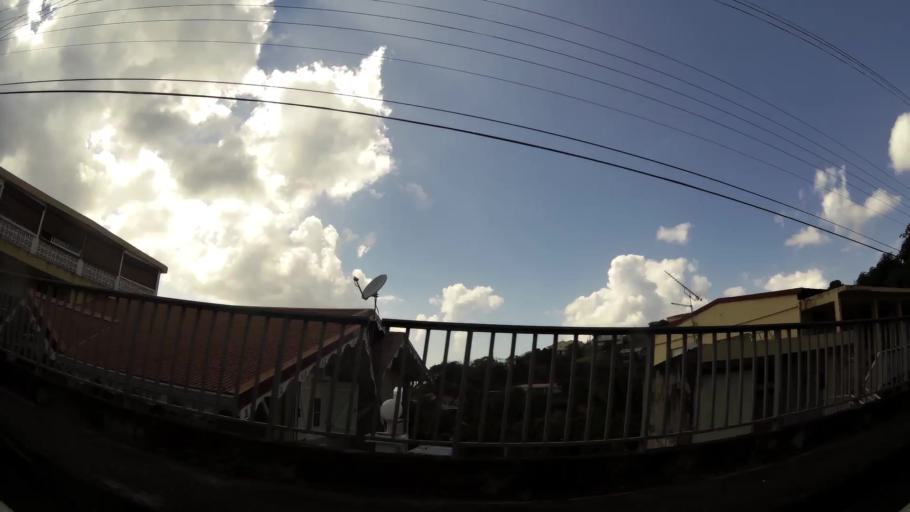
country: MQ
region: Martinique
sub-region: Martinique
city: Fort-de-France
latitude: 14.6284
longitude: -61.1146
